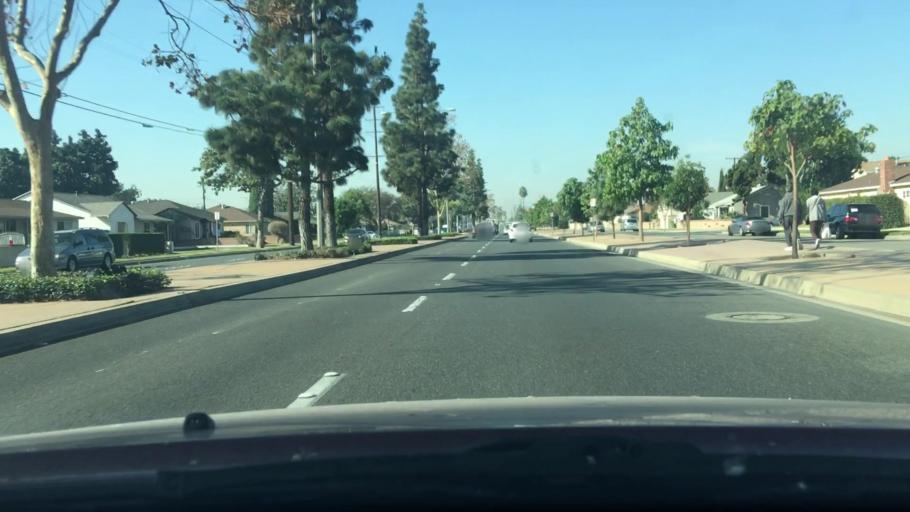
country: US
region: California
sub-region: Los Angeles County
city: Norwalk
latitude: 33.9022
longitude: -118.0940
